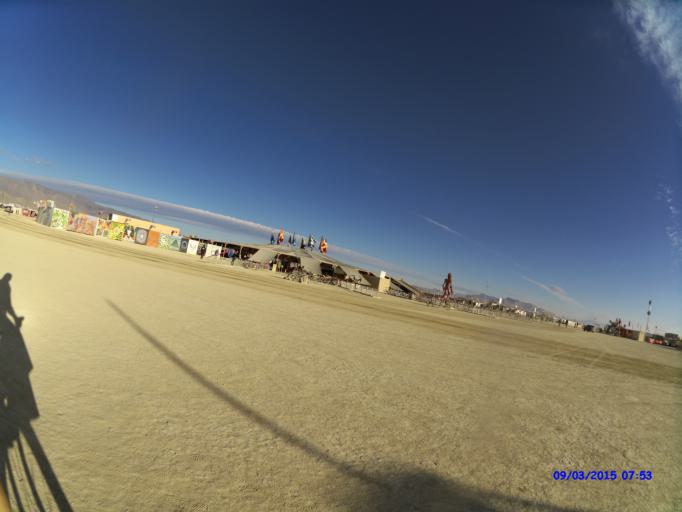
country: US
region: Nevada
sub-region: Pershing County
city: Lovelock
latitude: 40.7798
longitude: -119.2140
